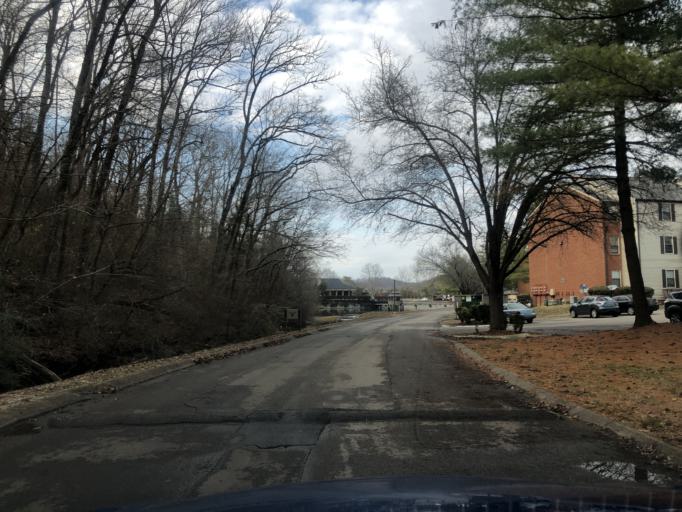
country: US
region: Tennessee
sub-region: Davidson County
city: Belle Meade
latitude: 36.0946
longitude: -86.9257
